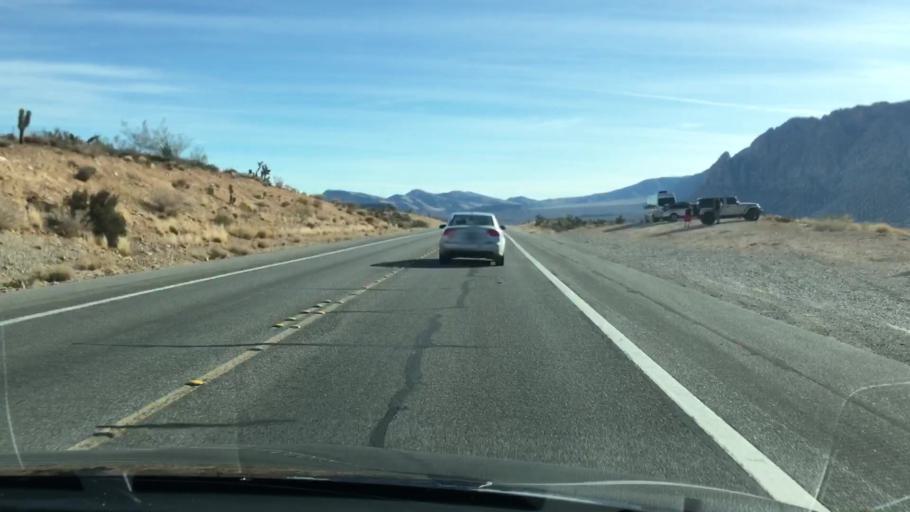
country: US
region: Nevada
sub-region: Clark County
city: Summerlin South
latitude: 36.1003
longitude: -115.4483
